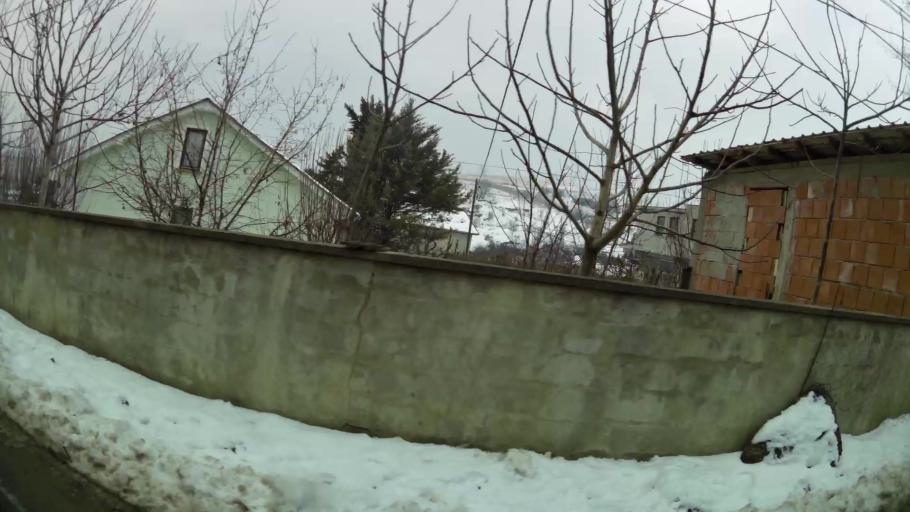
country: MK
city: Kondovo
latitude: 42.0315
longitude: 21.3383
